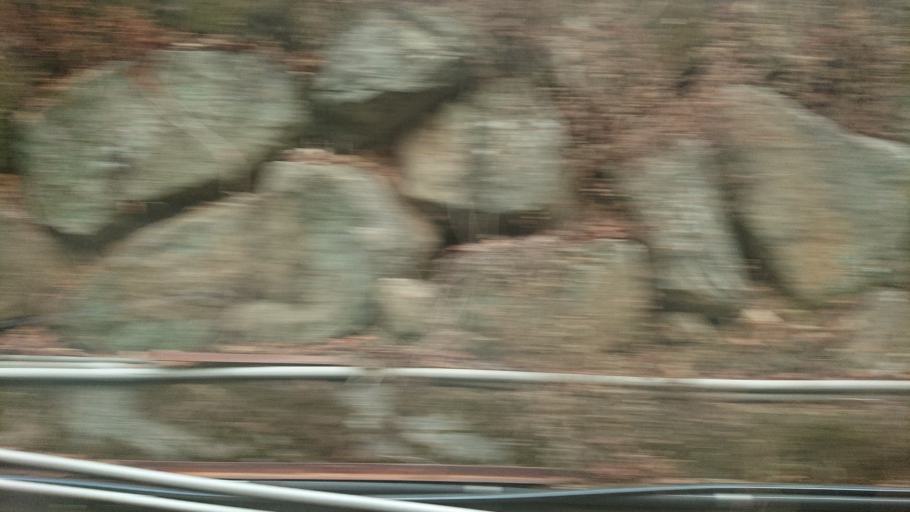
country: TW
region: Taiwan
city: Lugu
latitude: 23.6086
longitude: 120.7119
